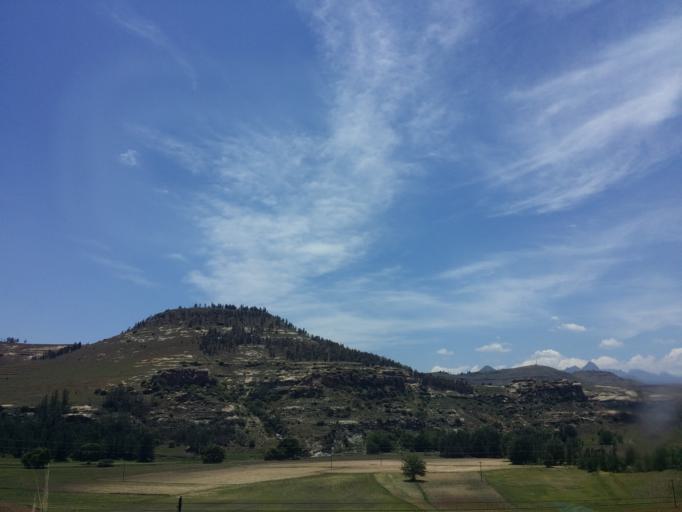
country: LS
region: Butha-Buthe
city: Butha-Buthe
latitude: -28.7257
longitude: 28.3880
